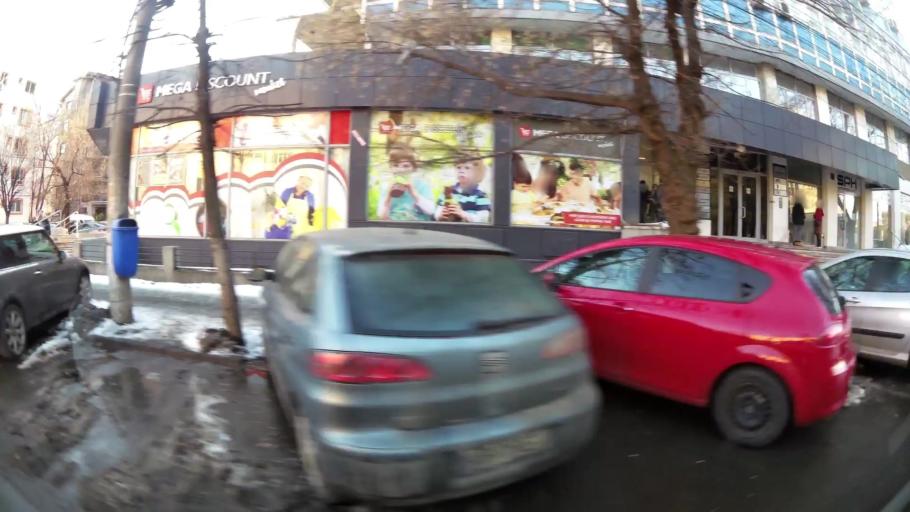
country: RO
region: Bucuresti
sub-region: Municipiul Bucuresti
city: Bucharest
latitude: 44.4474
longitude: 26.1328
